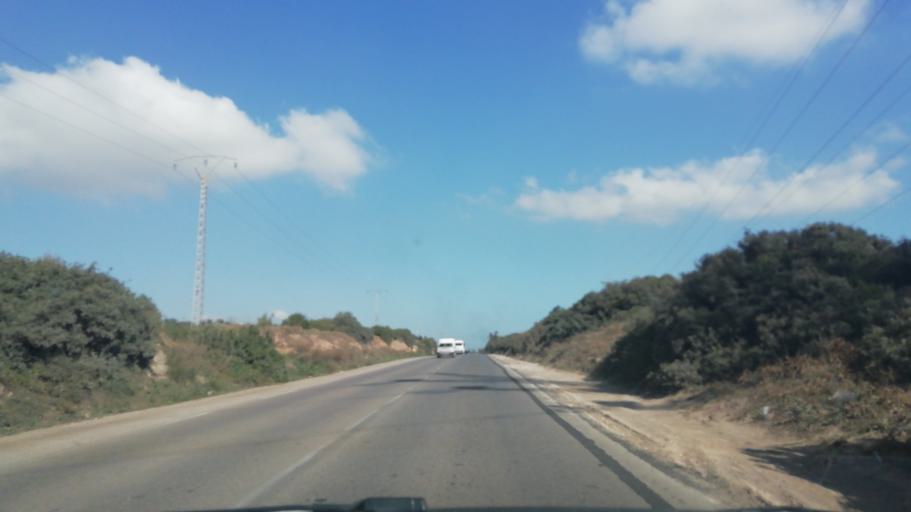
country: DZ
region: Oran
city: Ain el Bya
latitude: 35.7636
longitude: -0.2760
